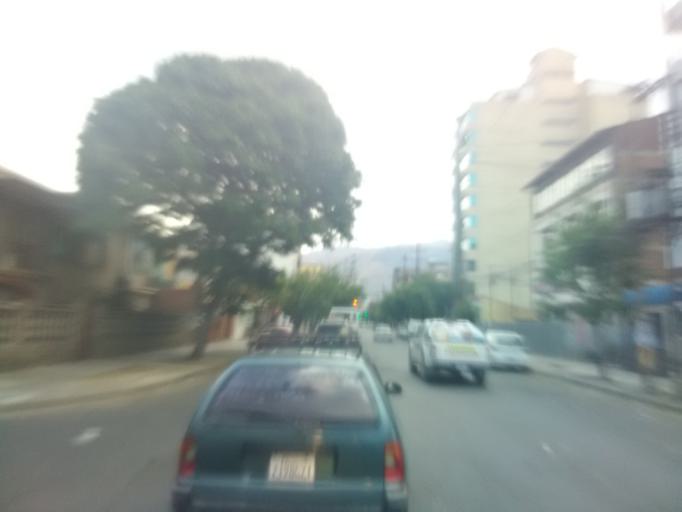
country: BO
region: Cochabamba
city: Cochabamba
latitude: -17.3975
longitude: -66.1488
